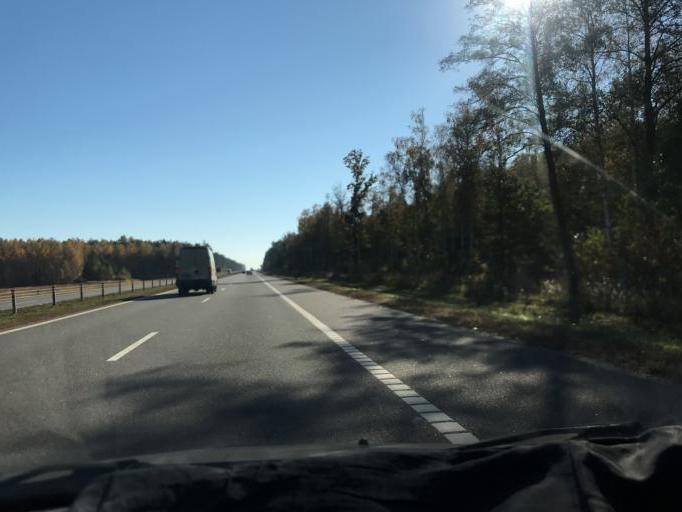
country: BY
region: Mogilev
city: Yalizava
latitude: 53.2654
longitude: 28.8855
